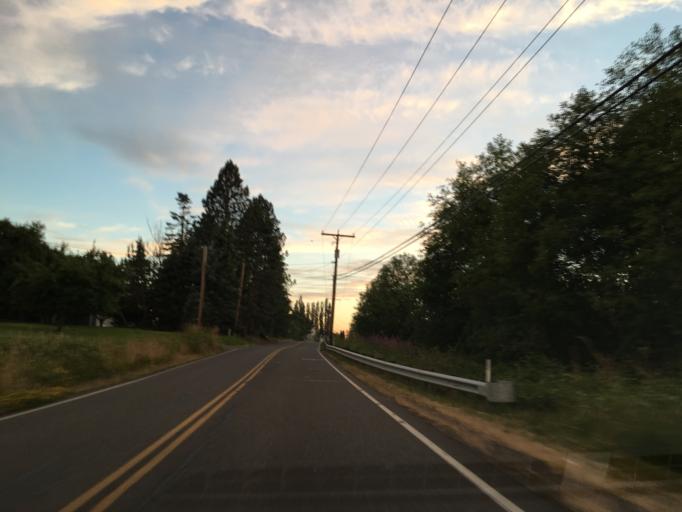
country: US
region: Washington
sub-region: Whatcom County
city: Bellingham
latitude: 48.7858
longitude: -122.4715
